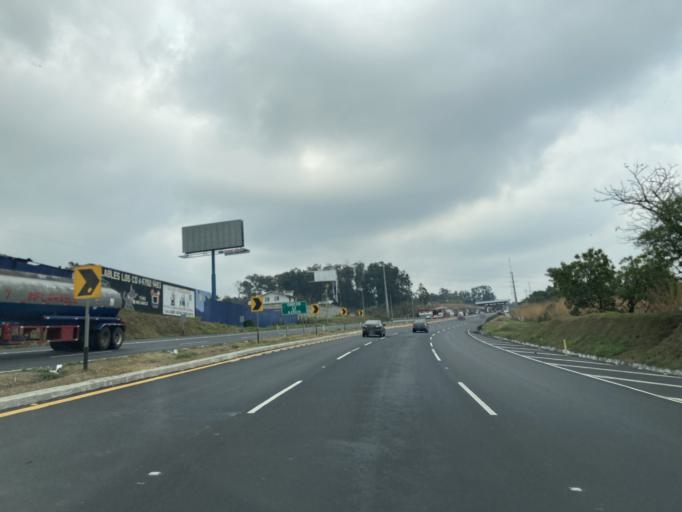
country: GT
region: Escuintla
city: Palin
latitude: 14.4062
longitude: -90.7058
